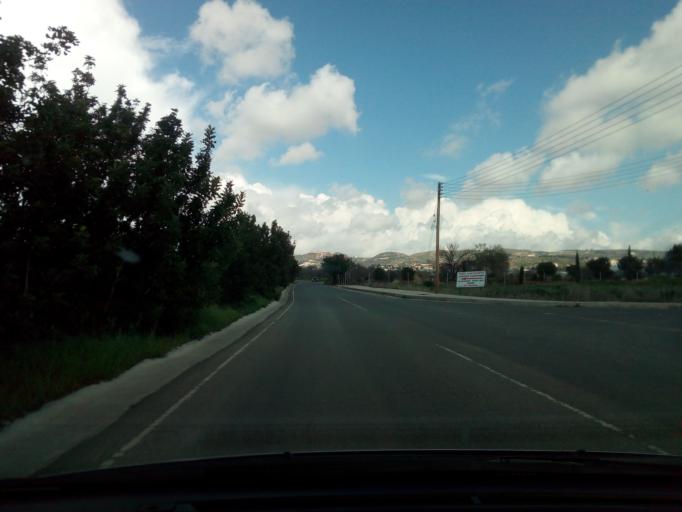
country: CY
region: Pafos
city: Mesogi
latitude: 34.8085
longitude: 32.4416
